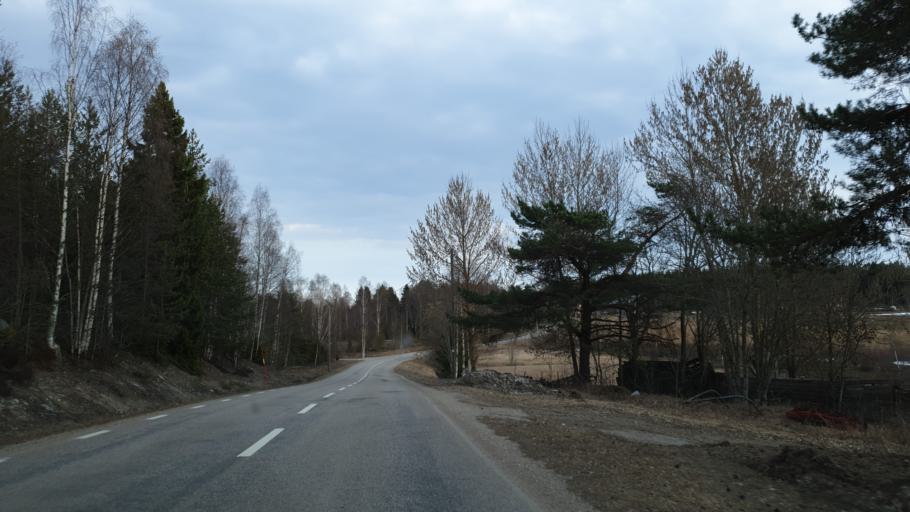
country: SE
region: Gaevleborg
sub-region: Nordanstigs Kommun
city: Bergsjoe
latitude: 61.9672
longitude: 17.3052
